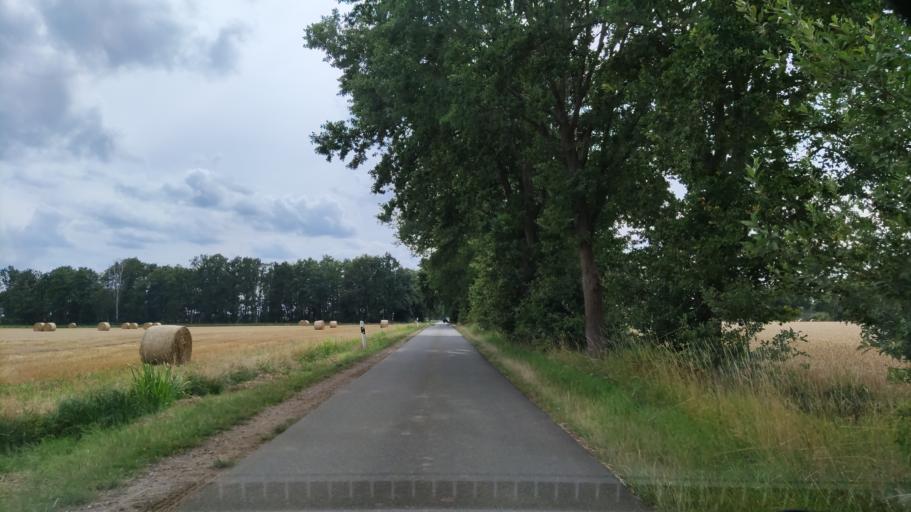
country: DE
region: Lower Saxony
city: Dannenberg
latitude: 53.0832
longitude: 11.1391
